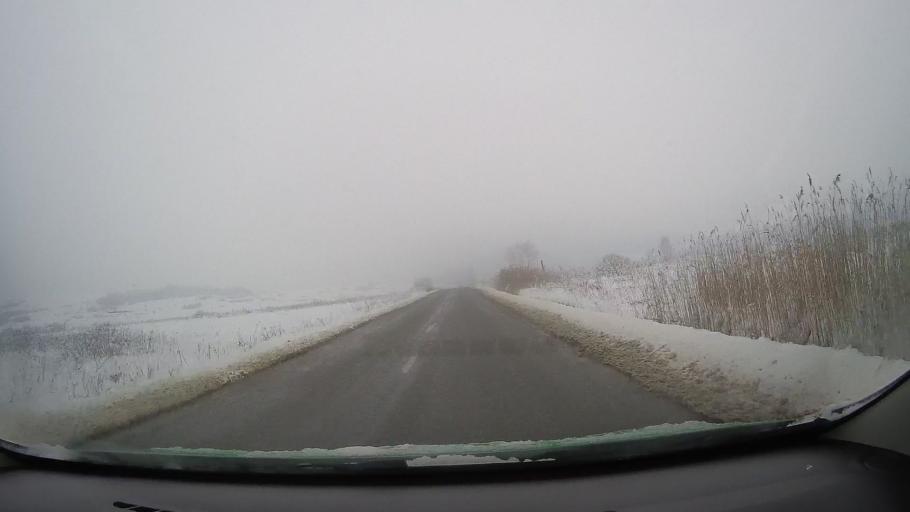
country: RO
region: Sibiu
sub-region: Comuna Orlat
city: Orlat
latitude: 45.7803
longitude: 23.9450
